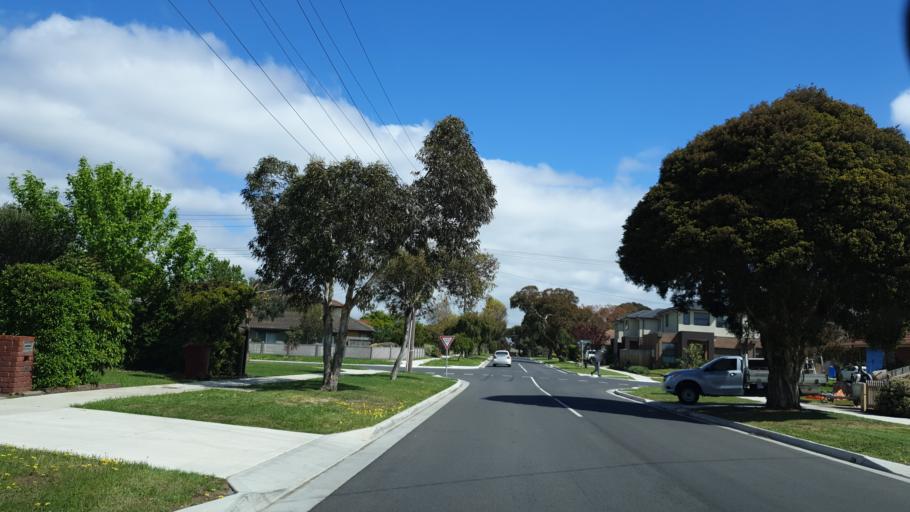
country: AU
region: Victoria
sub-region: Casey
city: Cranbourne
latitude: -38.1000
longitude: 145.2878
